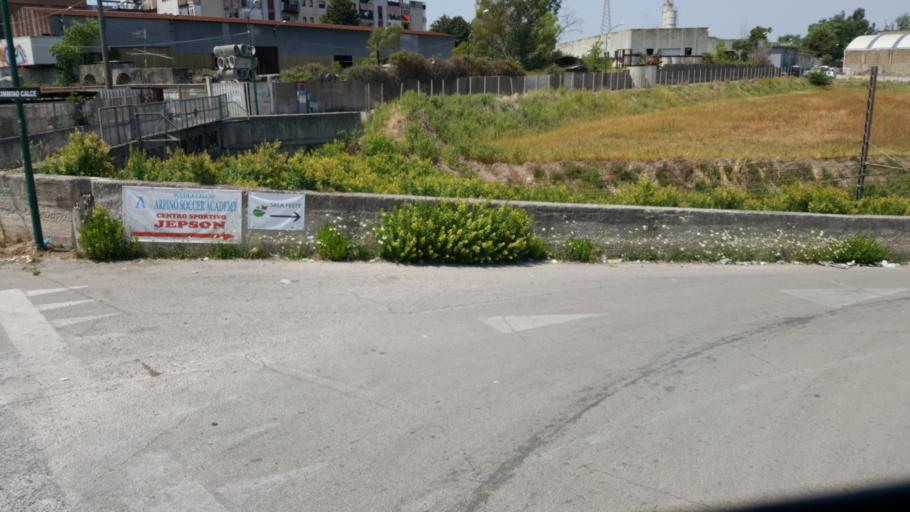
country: IT
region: Campania
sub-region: Provincia di Napoli
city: Arpino
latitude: 40.8842
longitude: 14.3134
